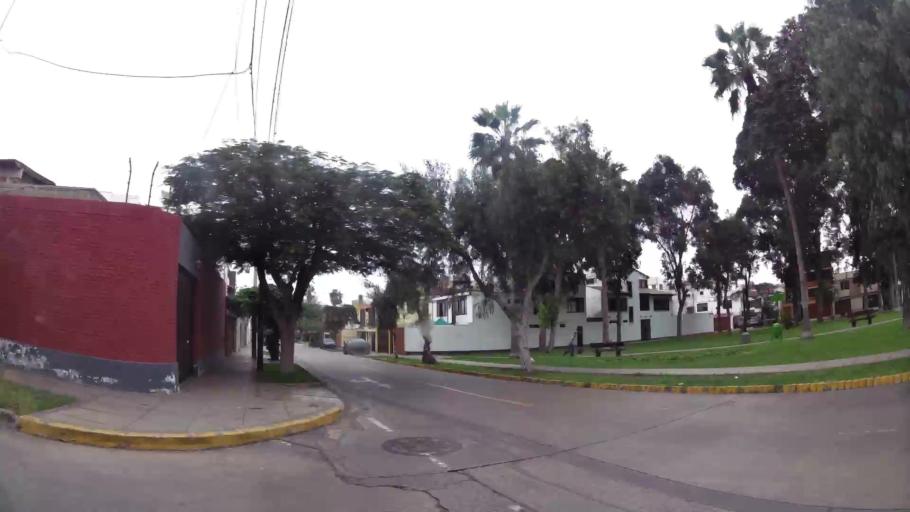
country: PE
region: Lima
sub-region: Lima
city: Surco
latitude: -12.1263
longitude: -76.9963
